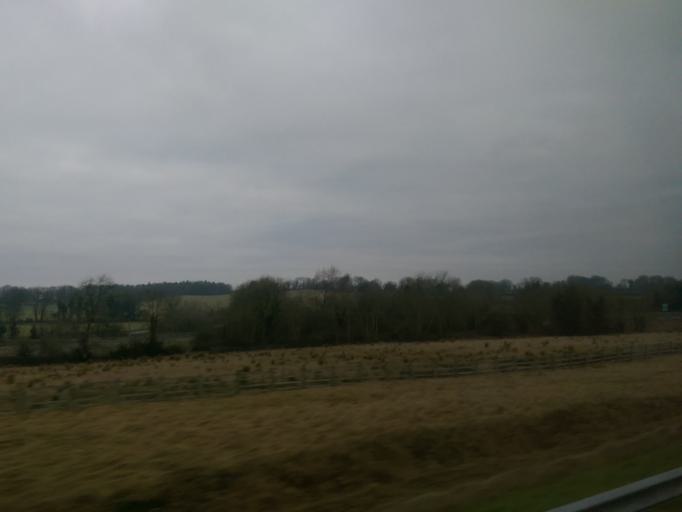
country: IE
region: Connaught
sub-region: County Galway
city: Ballinasloe
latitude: 53.3107
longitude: -8.2672
